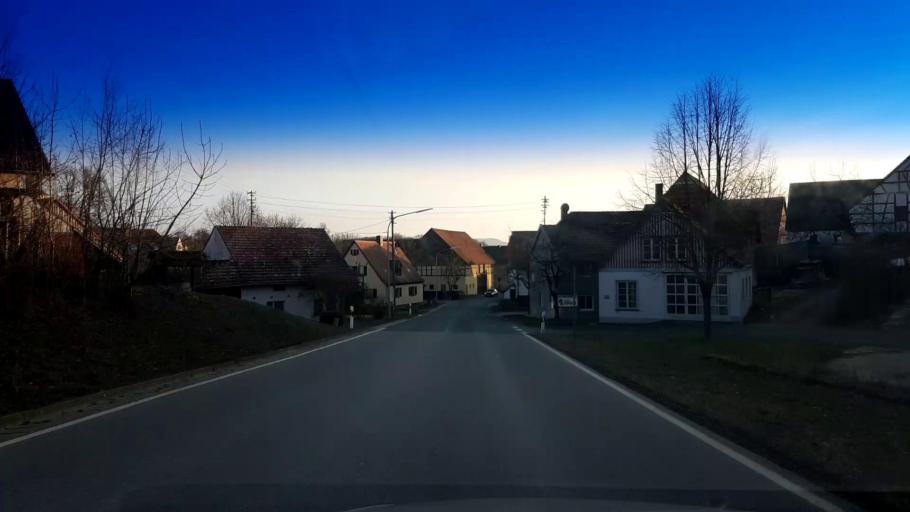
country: DE
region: Bavaria
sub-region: Upper Franconia
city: Schesslitz
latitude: 50.0057
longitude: 11.0160
